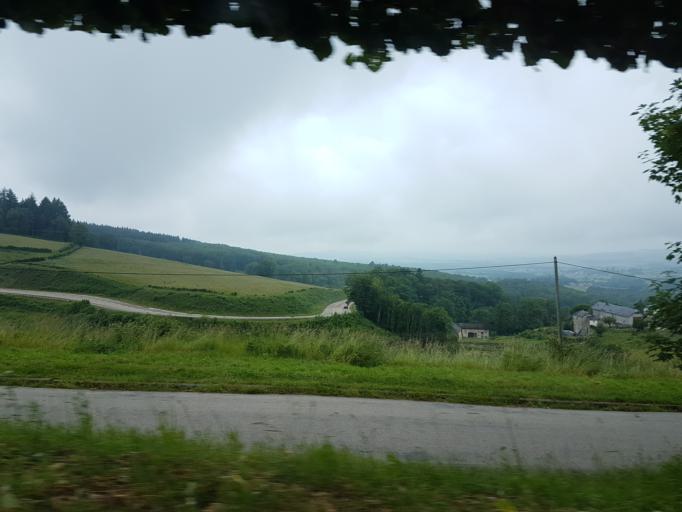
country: FR
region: Bourgogne
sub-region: Departement de la Nievre
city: Chateau-Chinon(Ville)
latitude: 47.0661
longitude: 3.9293
